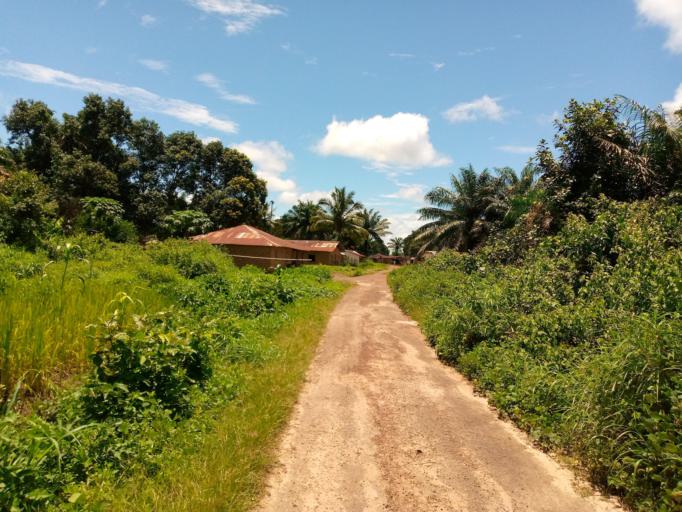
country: SL
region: Northern Province
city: Binkolo
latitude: 9.0569
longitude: -12.1523
